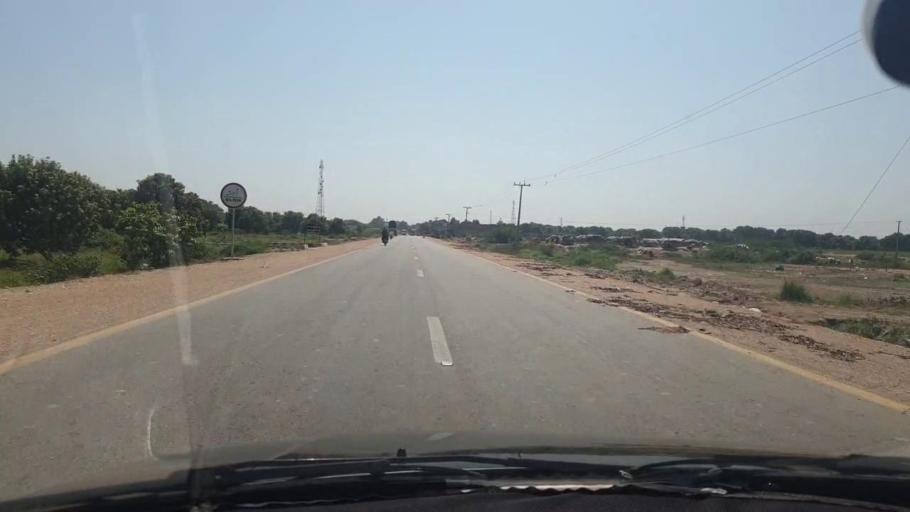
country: PK
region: Sindh
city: Chambar
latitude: 25.3048
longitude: 68.8087
